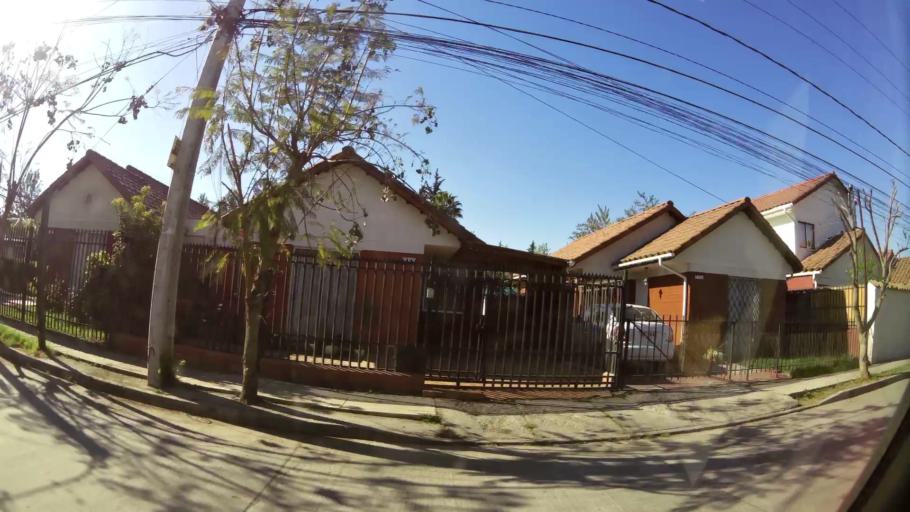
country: CL
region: Santiago Metropolitan
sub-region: Provincia de Talagante
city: Penaflor
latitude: -33.6013
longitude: -70.8751
